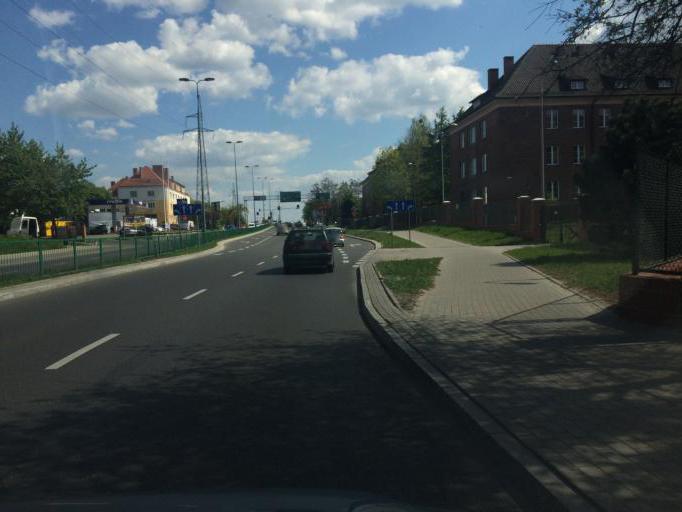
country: PL
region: Warmian-Masurian Voivodeship
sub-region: Olsztyn
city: Kortowo
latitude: 53.7677
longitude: 20.4622
